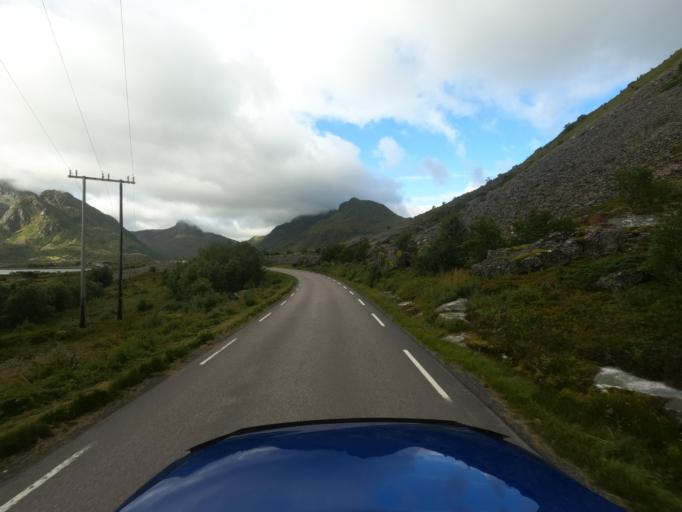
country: NO
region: Nordland
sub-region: Vestvagoy
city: Evjen
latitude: 68.1840
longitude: 13.8989
